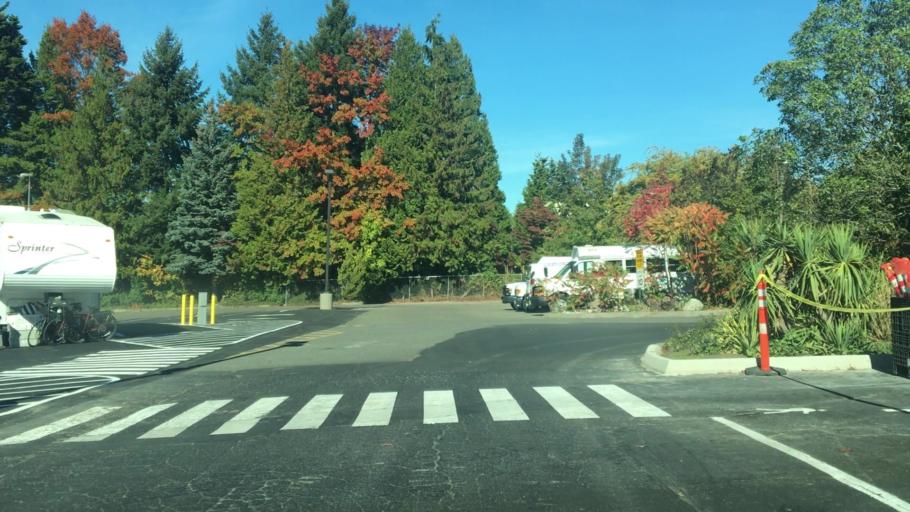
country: US
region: Washington
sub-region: King County
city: Yarrow Point
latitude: 47.6642
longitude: -122.2811
